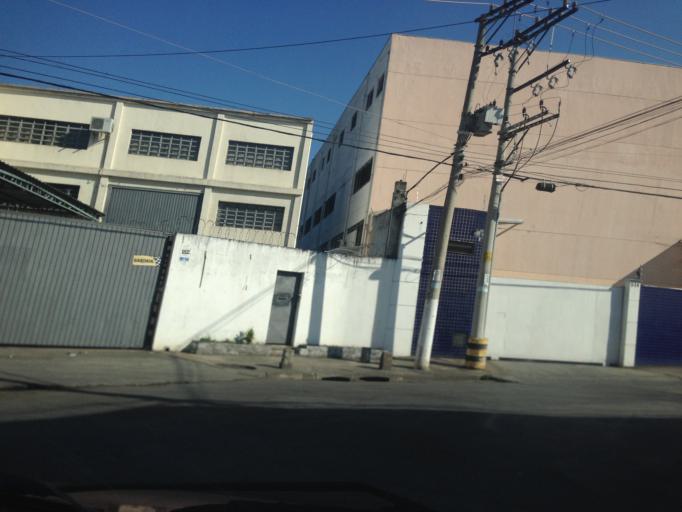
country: BR
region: Sao Paulo
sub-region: Sao Paulo
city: Sao Paulo
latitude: -23.5206
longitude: -46.6932
